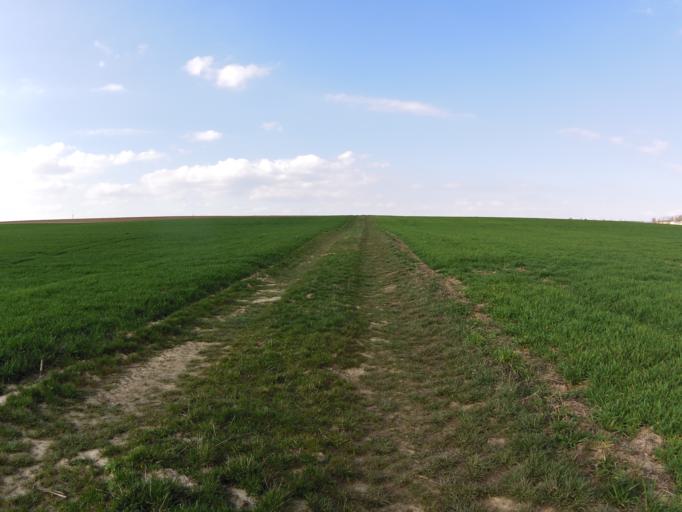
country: DE
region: Bavaria
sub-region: Regierungsbezirk Unterfranken
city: Biebelried
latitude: 49.7896
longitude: 10.0765
